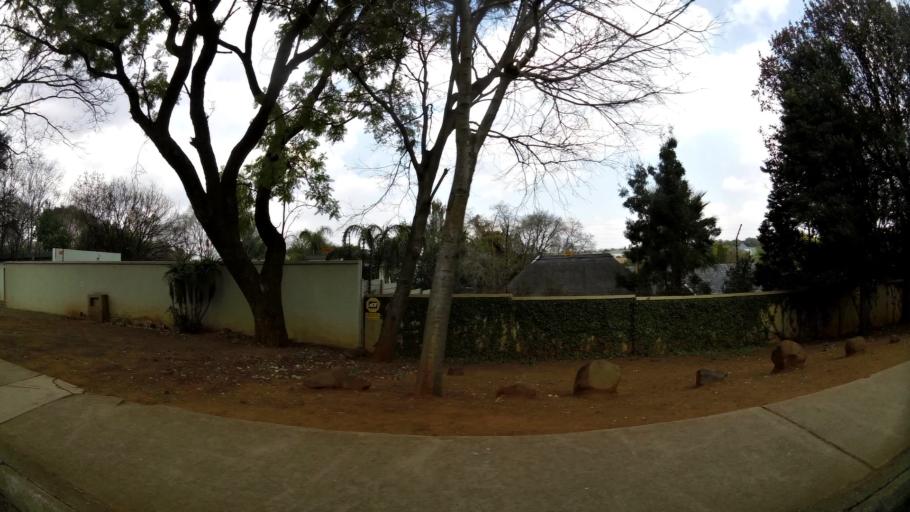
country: ZA
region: Gauteng
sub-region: City of Tshwane Metropolitan Municipality
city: Pretoria
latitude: -25.7629
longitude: 28.2831
